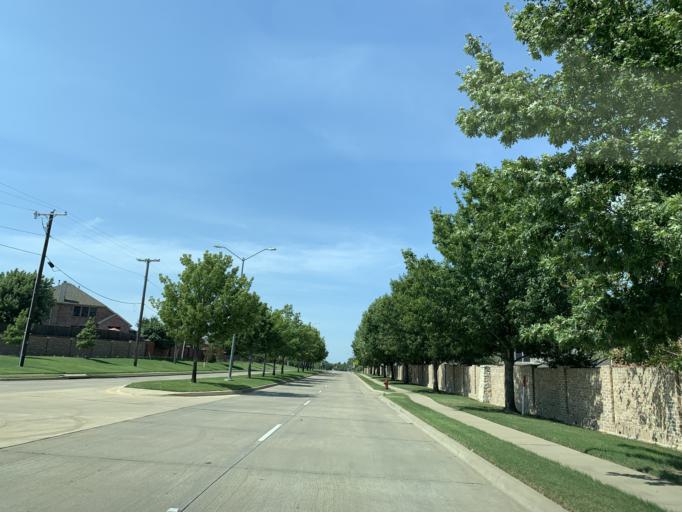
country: US
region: Texas
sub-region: Dallas County
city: Cedar Hill
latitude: 32.6474
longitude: -97.0069
